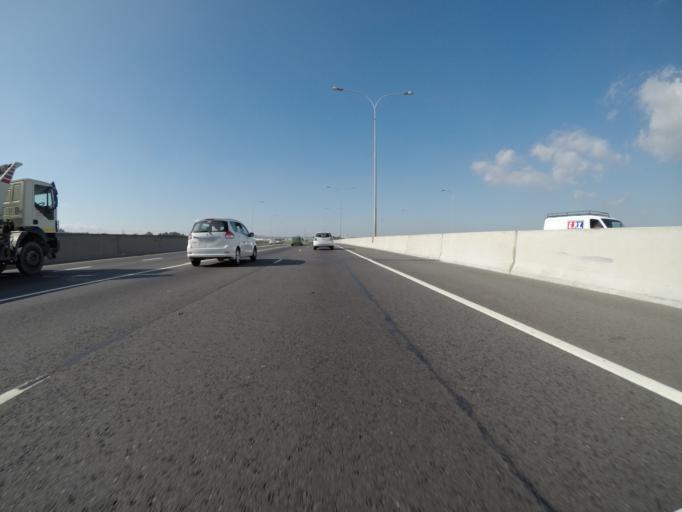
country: ZA
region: Western Cape
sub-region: City of Cape Town
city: Kraaifontein
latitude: -33.9187
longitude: 18.6659
